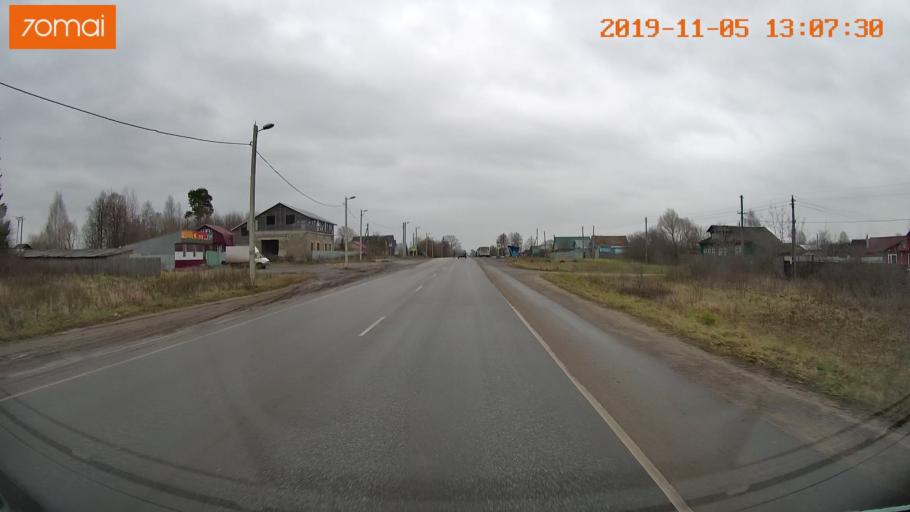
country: RU
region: Ivanovo
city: Kitovo
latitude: 56.8675
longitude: 41.2814
